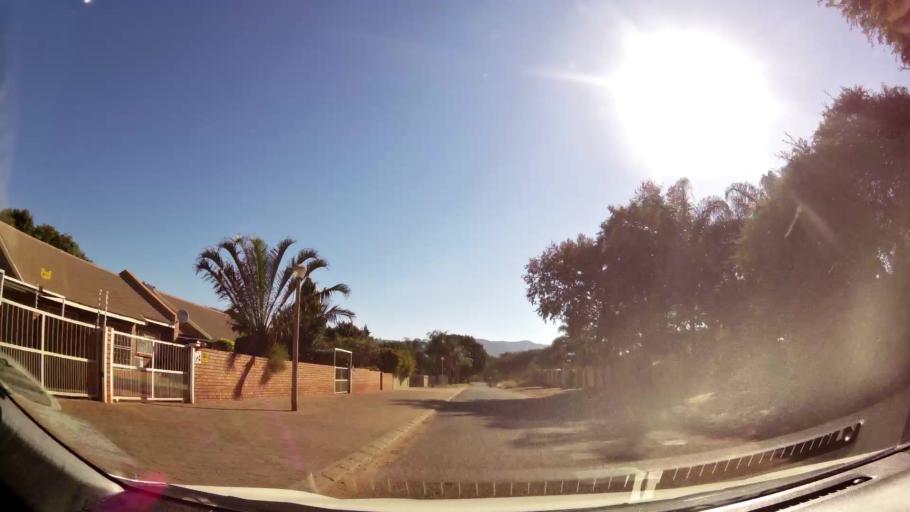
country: ZA
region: Limpopo
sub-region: Waterberg District Municipality
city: Mokopane
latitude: -24.2085
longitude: 28.9942
